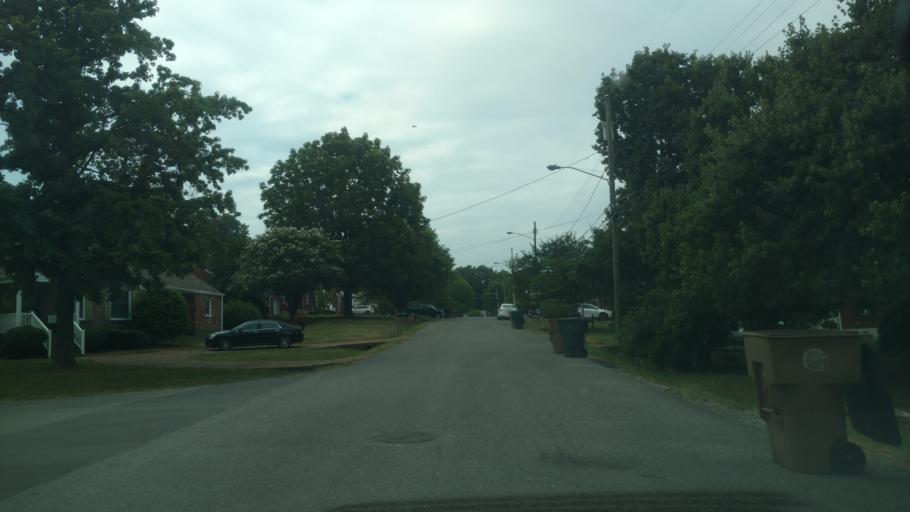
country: US
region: Tennessee
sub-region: Davidson County
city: Lakewood
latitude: 36.2096
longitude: -86.7067
